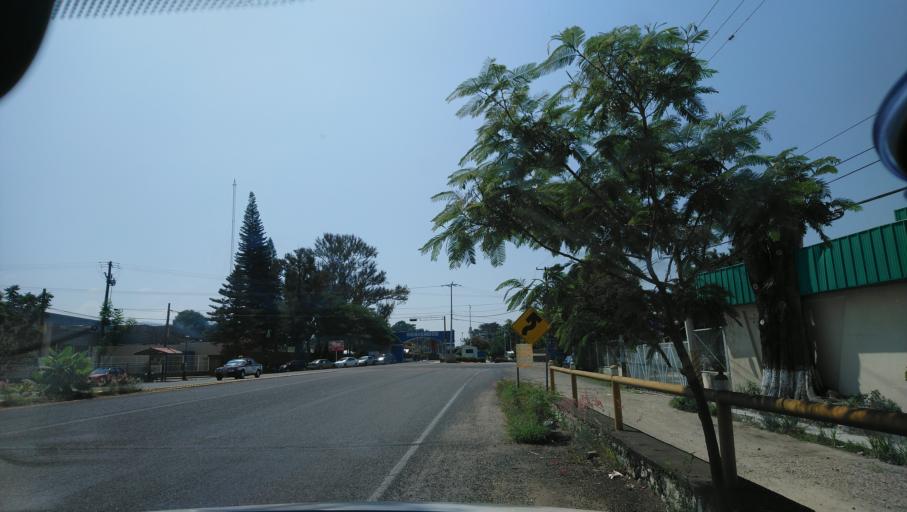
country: MX
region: Oaxaca
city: Santa Maria del Tule
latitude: 17.0476
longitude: -96.6397
